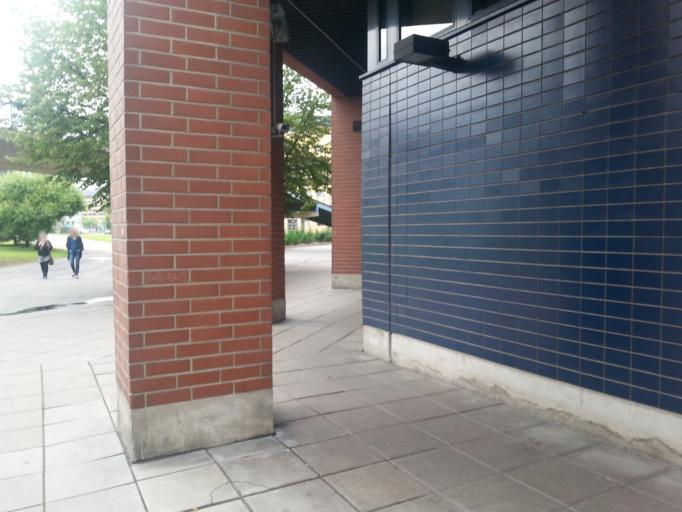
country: FI
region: Uusimaa
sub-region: Helsinki
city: Helsinki
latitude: 60.1798
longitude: 24.9586
